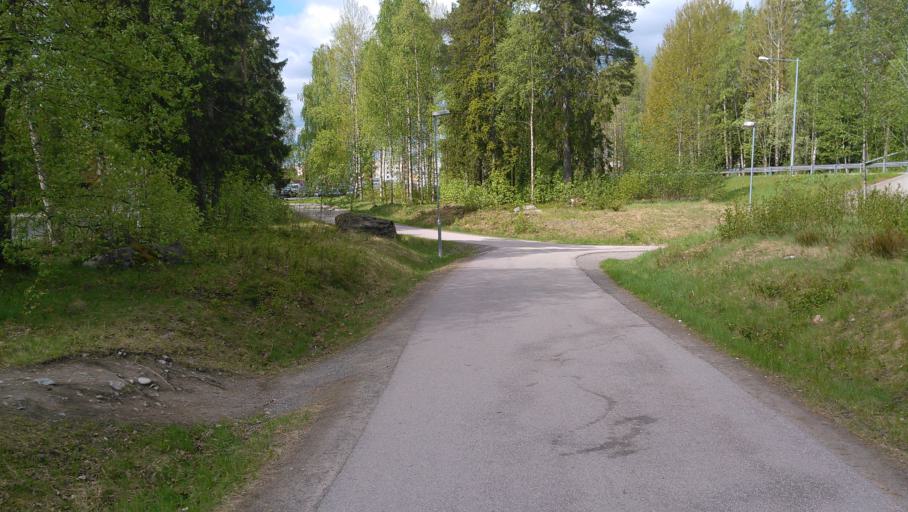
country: SE
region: Vaesterbotten
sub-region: Umea Kommun
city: Umea
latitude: 63.8139
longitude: 20.3132
